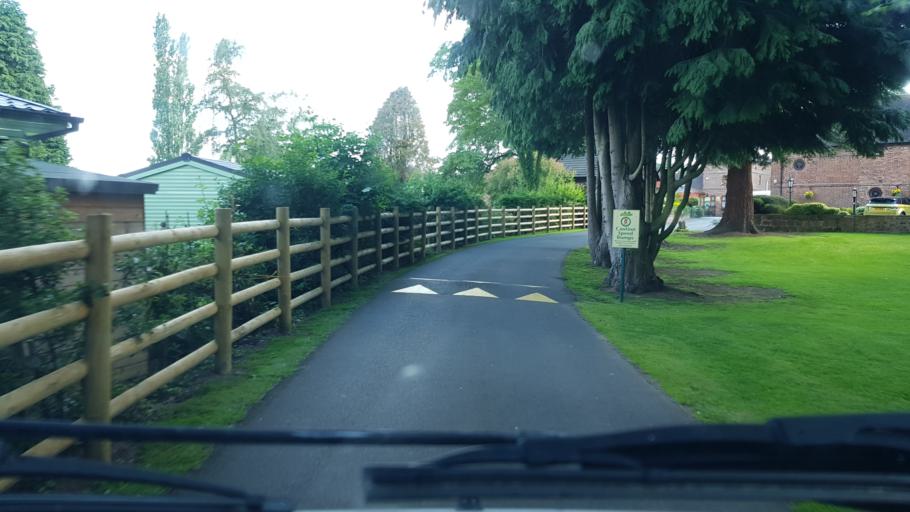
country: GB
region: England
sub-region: Worcestershire
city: Stourport-on-Severn
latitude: 52.3443
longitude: -2.2987
